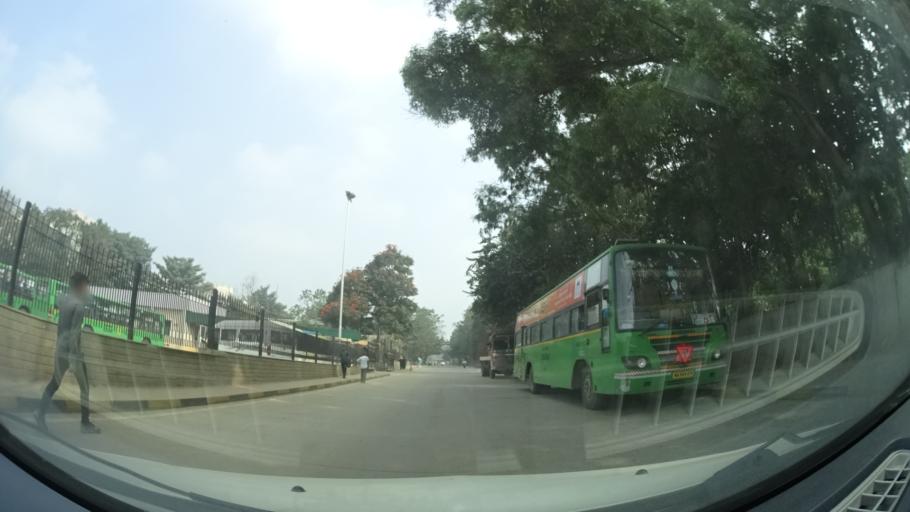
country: IN
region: Karnataka
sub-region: Bangalore Urban
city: Anekal
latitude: 12.8359
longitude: 77.6574
